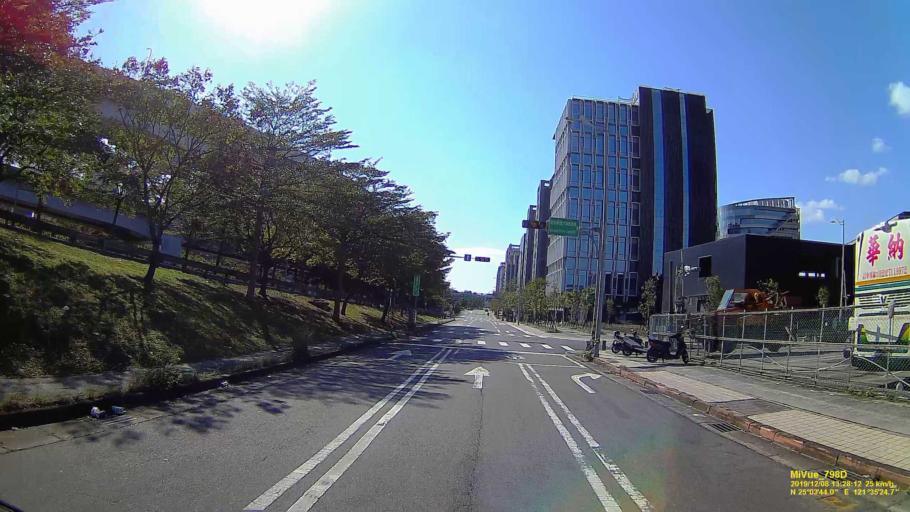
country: TW
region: Taipei
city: Taipei
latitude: 25.0621
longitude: 121.5900
